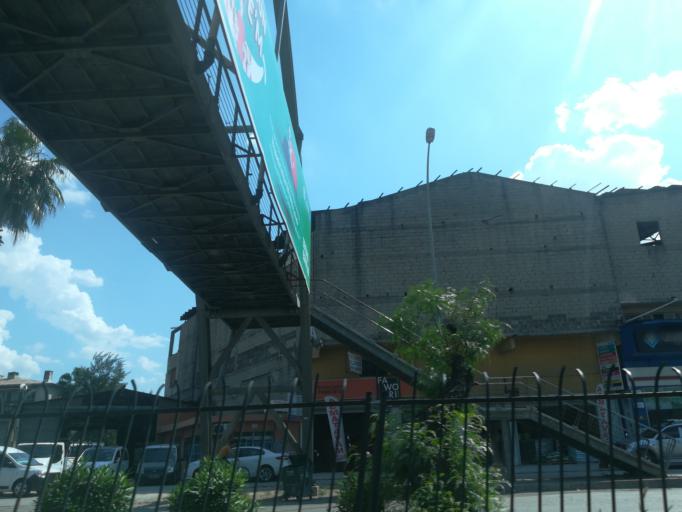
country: TR
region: Adana
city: Adana
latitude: 36.9894
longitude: 35.3414
